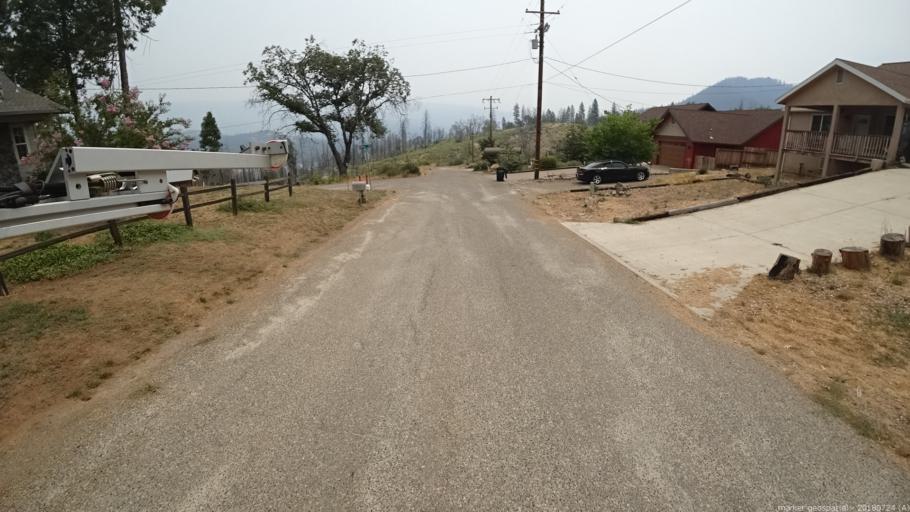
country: US
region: California
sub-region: Madera County
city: Oakhurst
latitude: 37.3165
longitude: -119.5836
